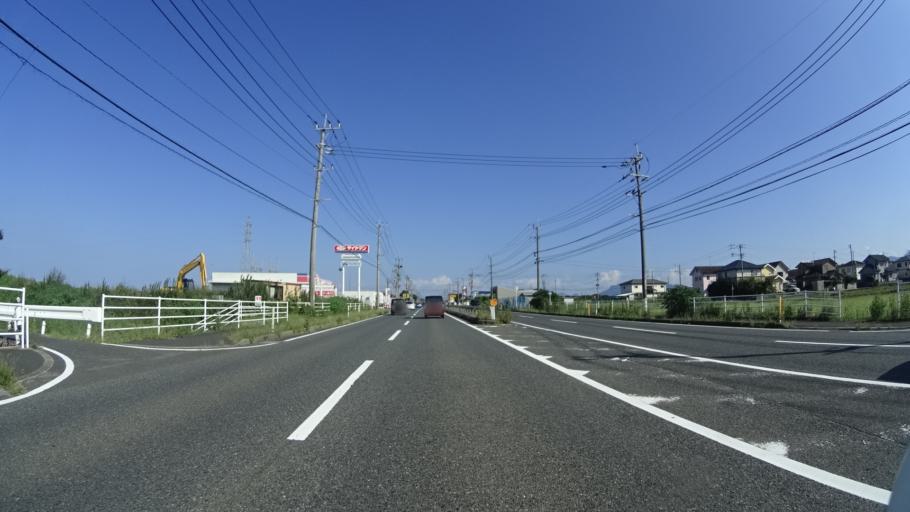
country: JP
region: Fukuoka
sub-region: Buzen-shi
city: Buzen
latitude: 33.5948
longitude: 131.1416
